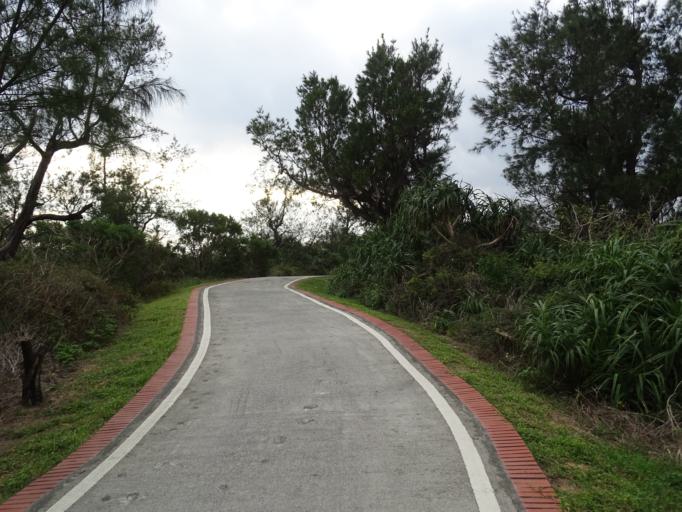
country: TW
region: Taiwan
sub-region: Keelung
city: Keelung
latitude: 25.0242
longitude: 121.9375
